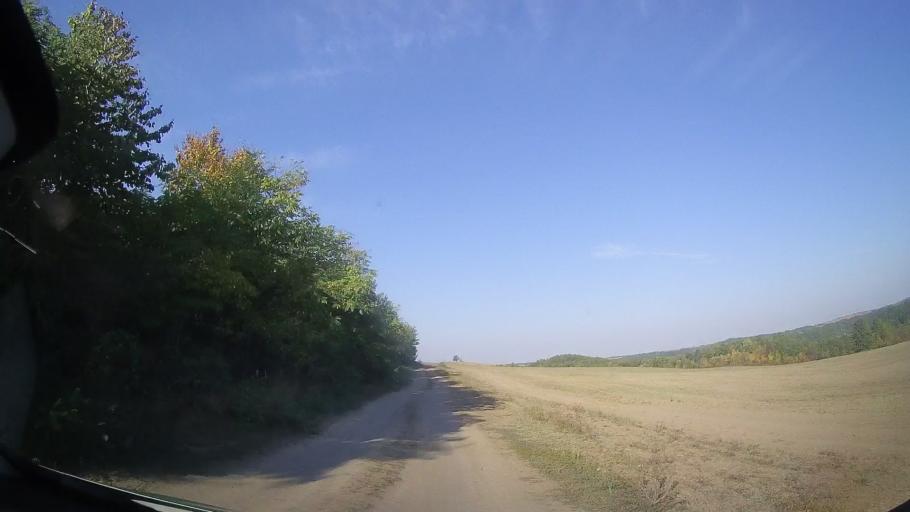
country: RO
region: Timis
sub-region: Comuna Bogda
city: Bogda
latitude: 45.9089
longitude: 21.5944
